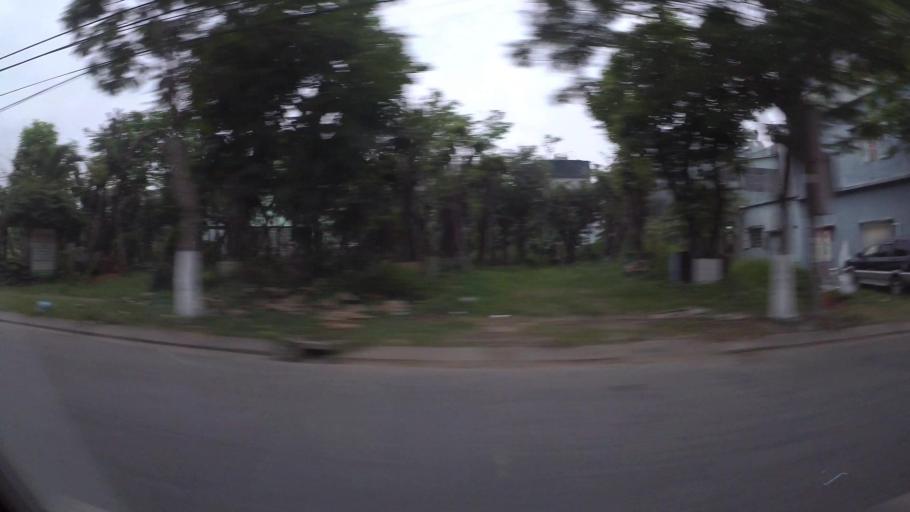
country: VN
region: Da Nang
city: Thanh Khe
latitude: 16.0508
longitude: 108.1784
